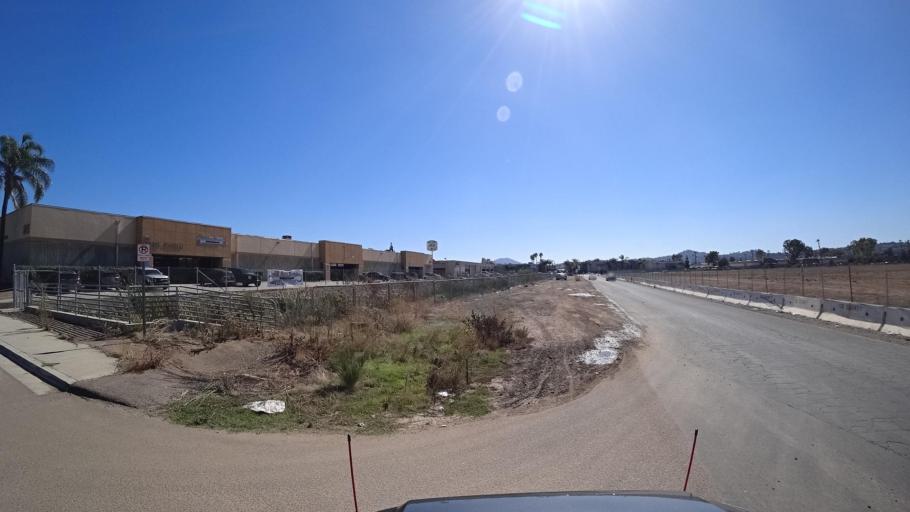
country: US
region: California
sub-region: San Diego County
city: Santee
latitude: 32.8205
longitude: -116.9650
